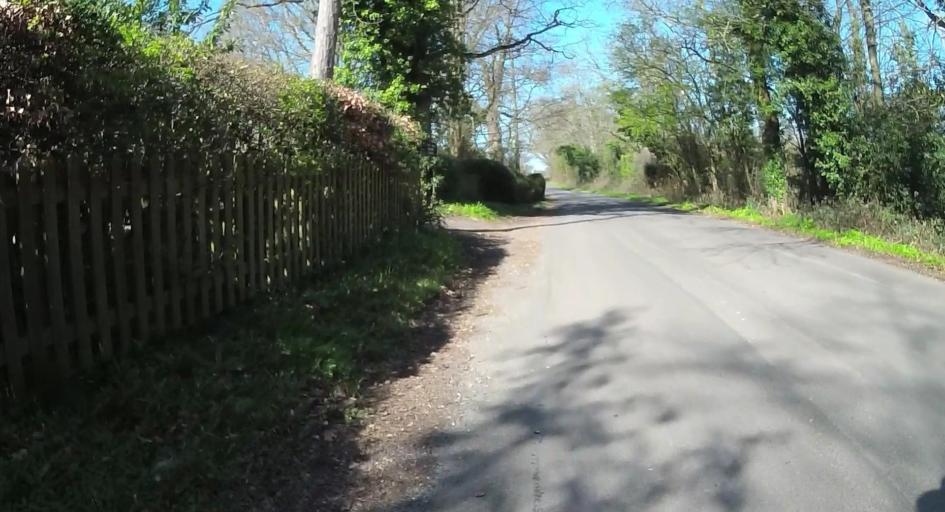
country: GB
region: England
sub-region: West Berkshire
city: Thatcham
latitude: 51.4041
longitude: -1.1989
